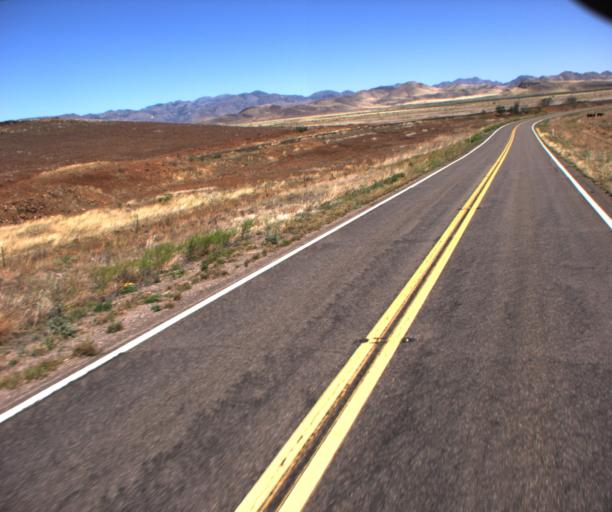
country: US
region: Arizona
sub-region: Cochise County
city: Douglas
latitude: 31.6174
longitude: -109.2150
